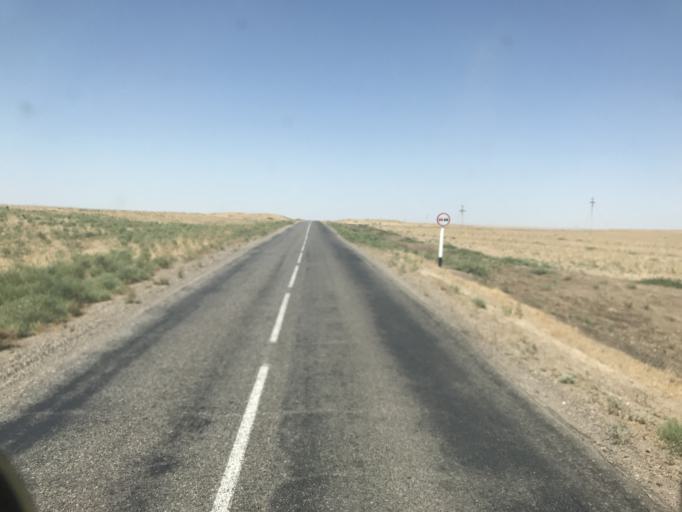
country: UZ
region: Toshkent
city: Chinoz
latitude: 41.1574
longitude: 68.6660
